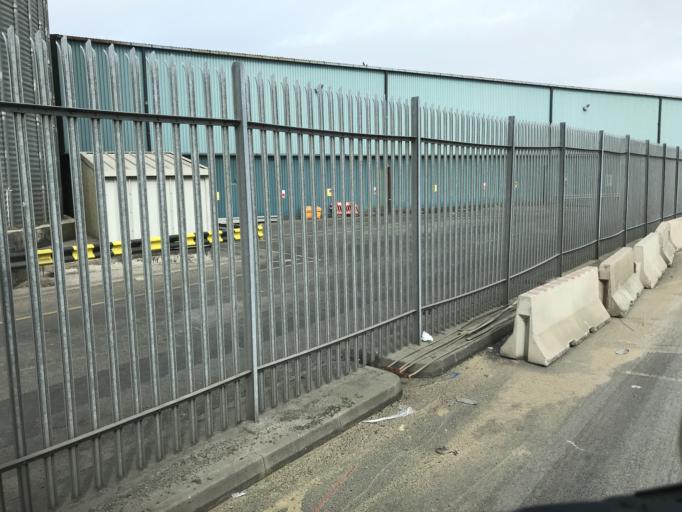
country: GB
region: England
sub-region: Sefton
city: Bootle
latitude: 53.4585
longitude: -3.0171
